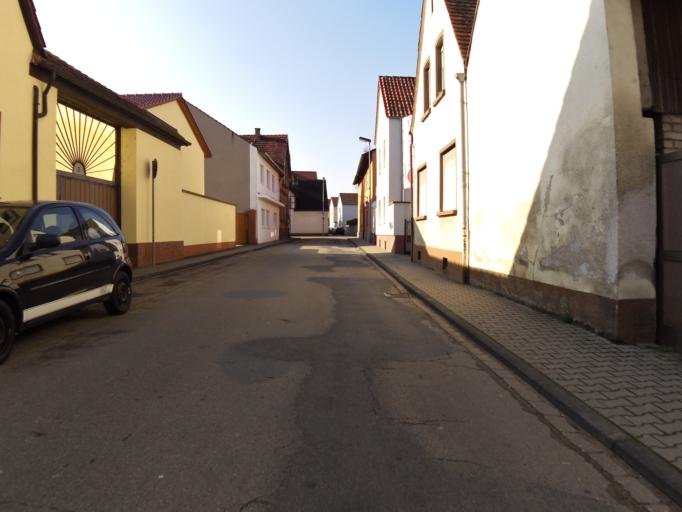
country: DE
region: Rheinland-Pfalz
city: Bobenheim-Roxheim
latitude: 49.5883
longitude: 8.3593
